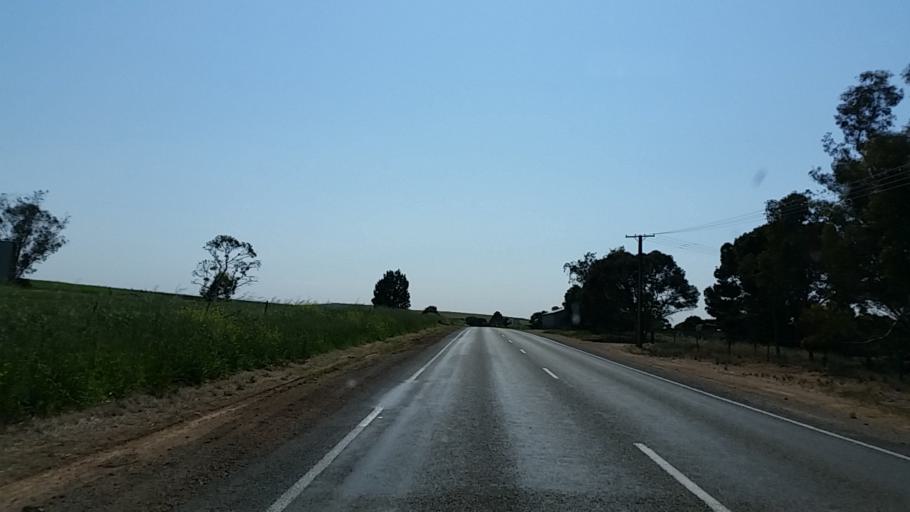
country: AU
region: South Australia
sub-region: Port Pirie City and Dists
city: Crystal Brook
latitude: -33.2562
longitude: 138.3597
